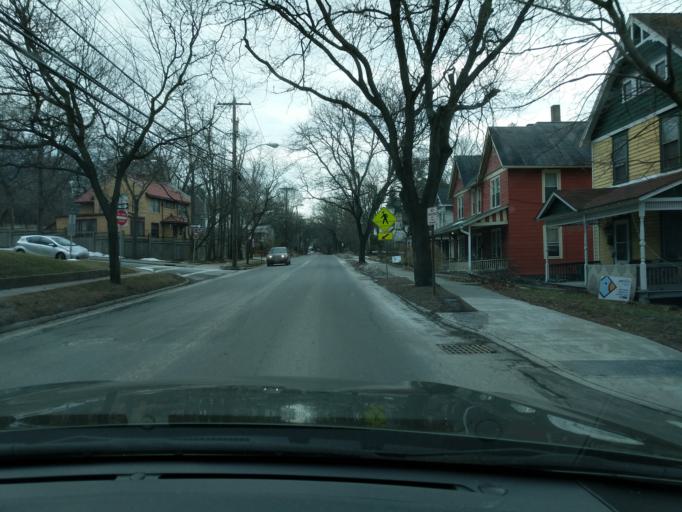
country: US
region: New York
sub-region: Tompkins County
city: East Ithaca
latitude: 42.4366
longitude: -76.4853
